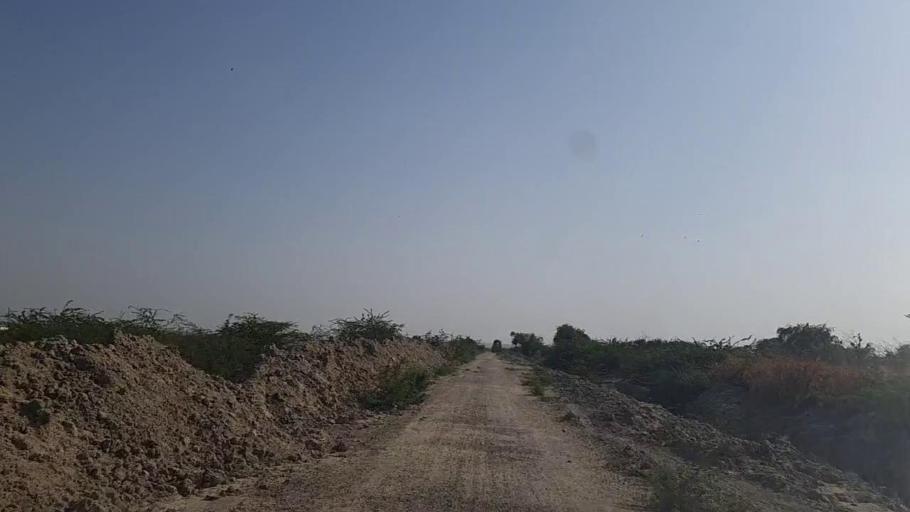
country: PK
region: Sindh
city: Kadhan
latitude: 24.5799
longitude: 69.2628
